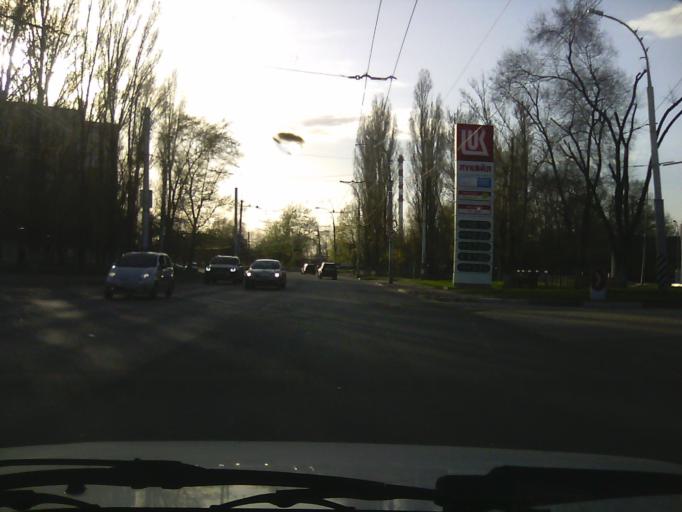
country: RU
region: Saratov
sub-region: Saratovskiy Rayon
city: Saratov
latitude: 51.5912
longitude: 45.9488
